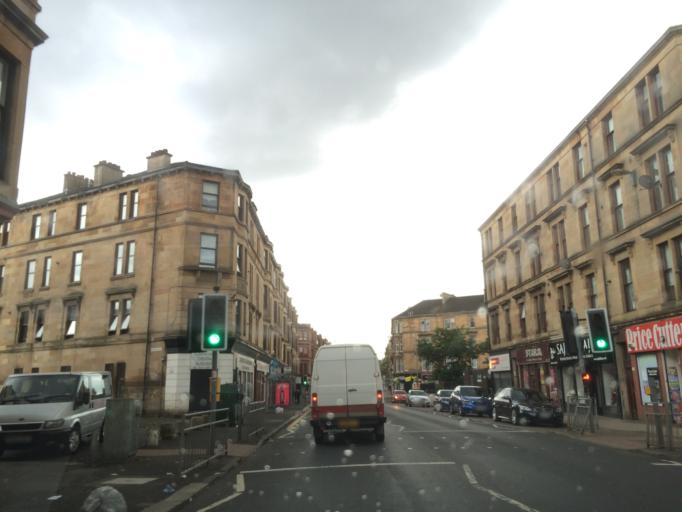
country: GB
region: Scotland
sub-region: Glasgow City
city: Glasgow
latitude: 55.8361
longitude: -4.2568
